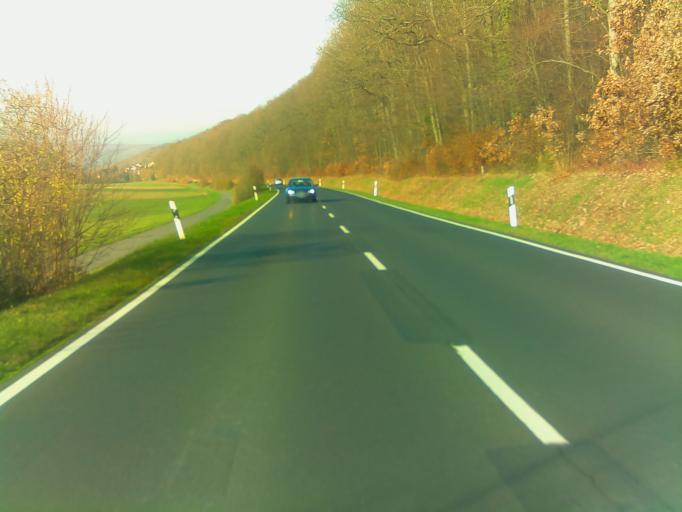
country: DE
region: Bavaria
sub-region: Regierungsbezirk Unterfranken
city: Hafenlohr
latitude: 49.8749
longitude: 9.6066
